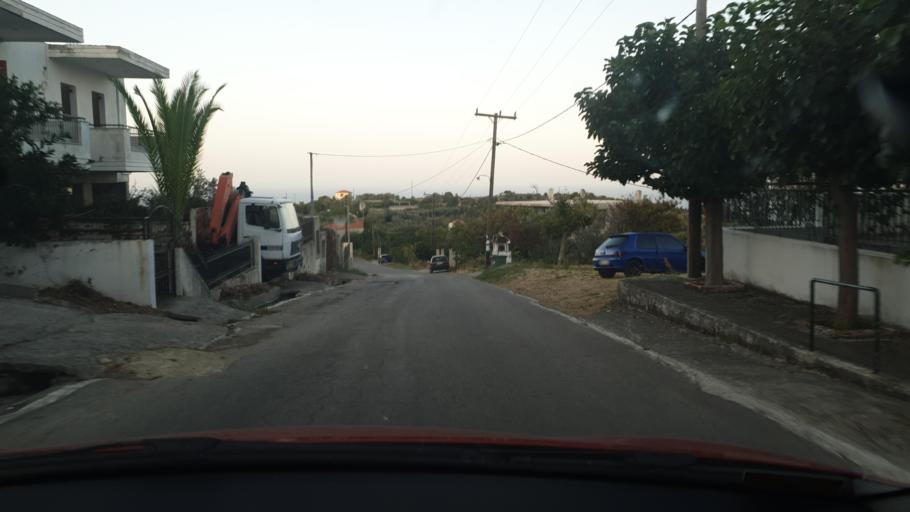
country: GR
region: Central Greece
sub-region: Nomos Evvoias
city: Oxilithos
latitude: 38.5865
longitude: 24.1127
